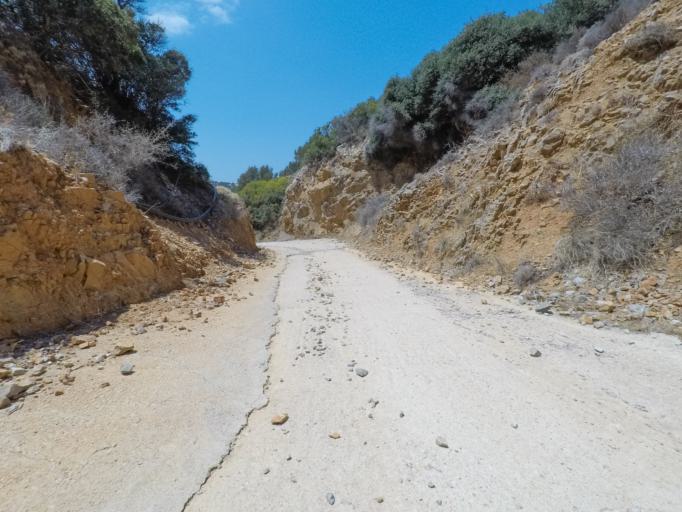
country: GR
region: Crete
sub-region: Nomos Lasithiou
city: Elounda
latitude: 35.3147
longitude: 25.7378
